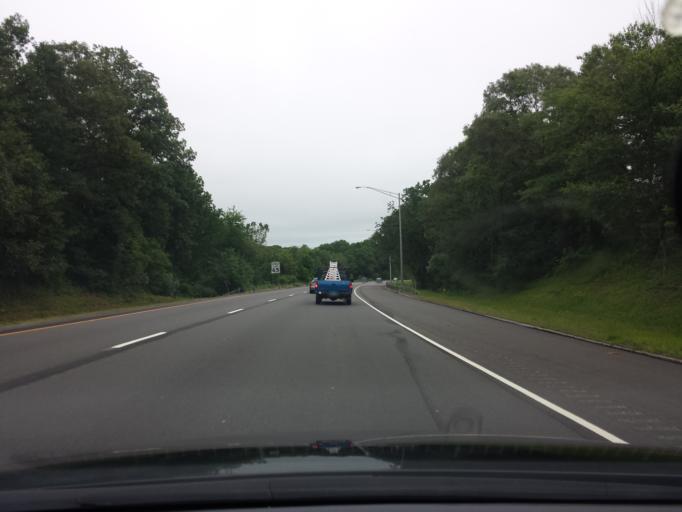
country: US
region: Connecticut
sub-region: New London County
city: Mystic
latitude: 41.3716
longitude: -71.9953
